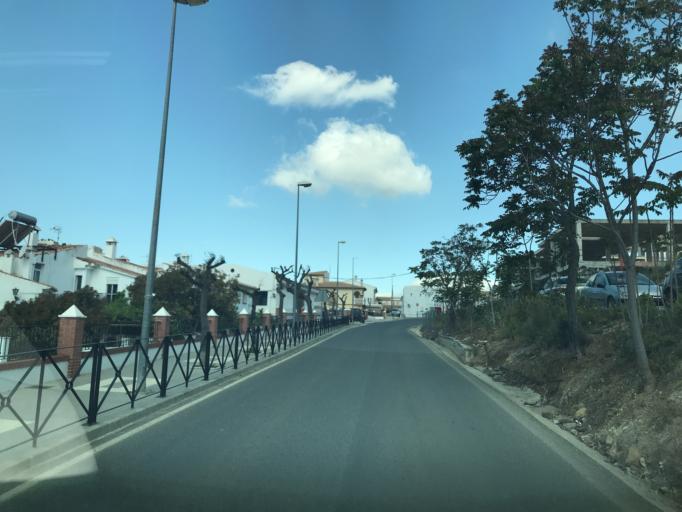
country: ES
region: Andalusia
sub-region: Provincia de Malaga
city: Periana
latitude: 36.9272
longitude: -4.1871
